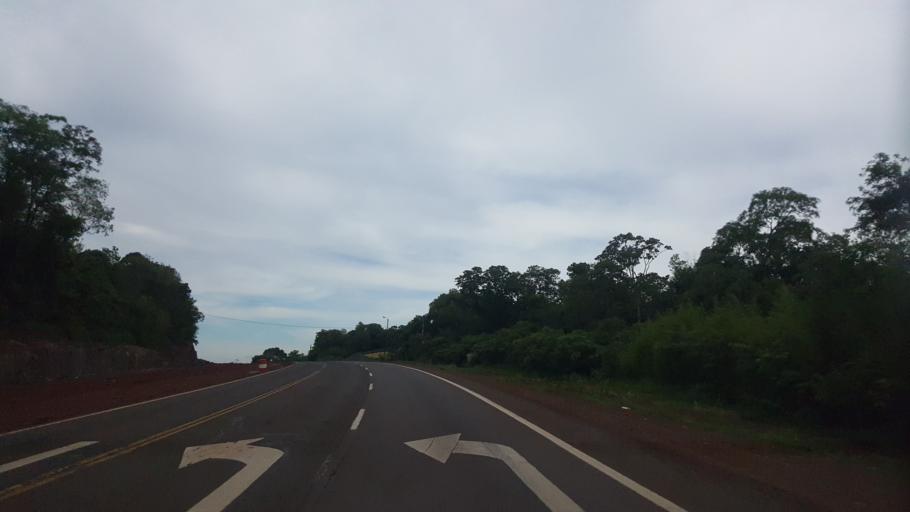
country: AR
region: Misiones
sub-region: Departamento de Candelaria
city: Loreto
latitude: -27.3520
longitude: -55.5492
